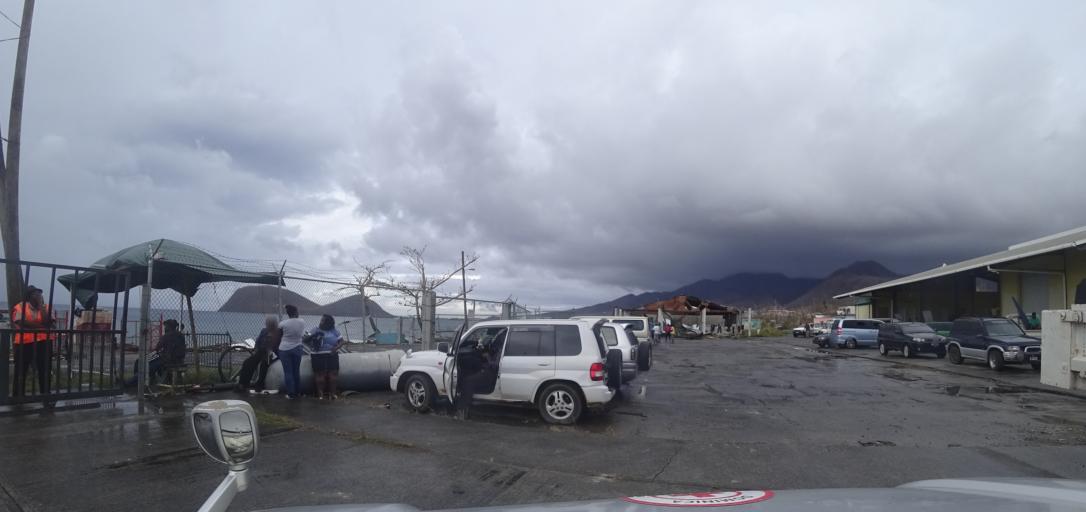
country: DM
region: Saint John
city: Portsmouth
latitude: 15.5631
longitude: -61.4590
